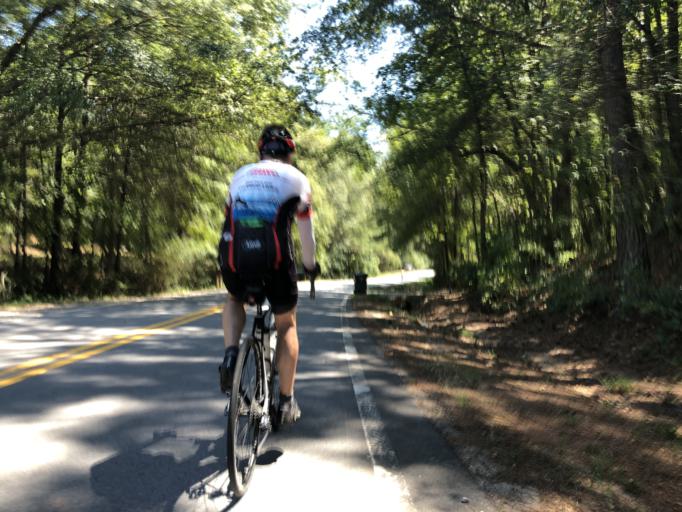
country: US
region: Georgia
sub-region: Fulton County
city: Chattahoochee Hills
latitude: 33.4941
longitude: -84.8196
